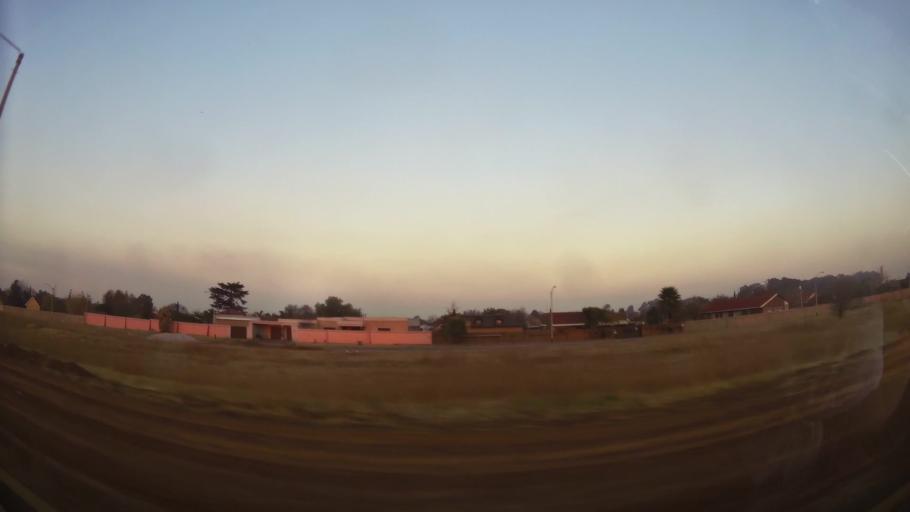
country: ZA
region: Gauteng
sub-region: Ekurhuleni Metropolitan Municipality
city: Springs
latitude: -26.3456
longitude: 28.4159
